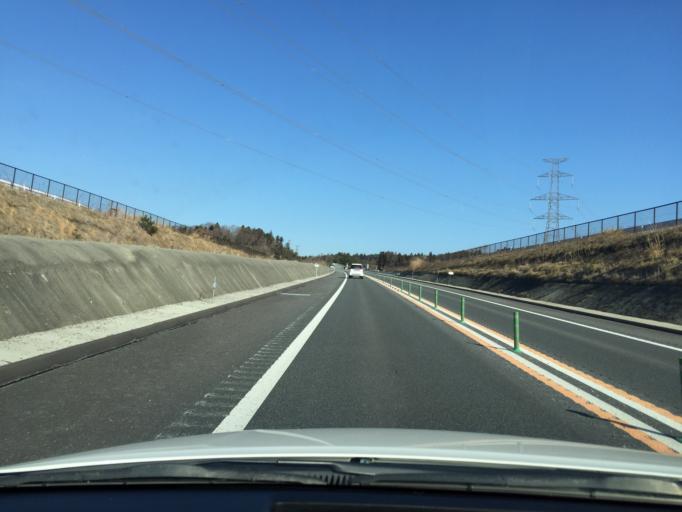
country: JP
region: Fukushima
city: Namie
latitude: 37.5138
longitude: 140.9438
